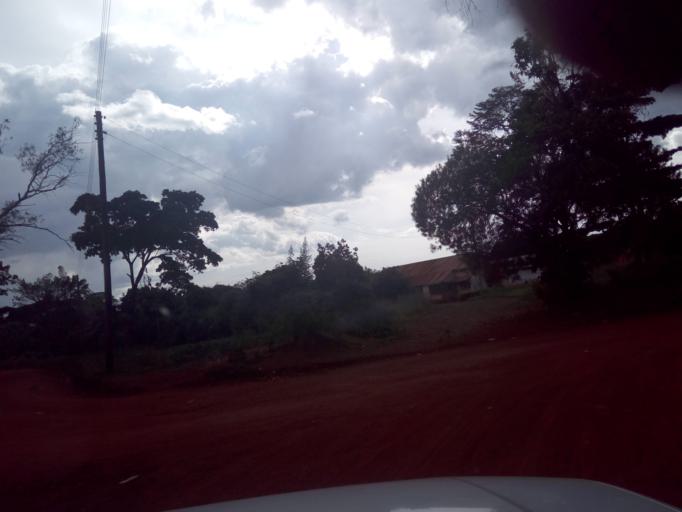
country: UG
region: Western Region
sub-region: Masindi District
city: Masindi
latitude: 1.6916
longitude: 31.7191
